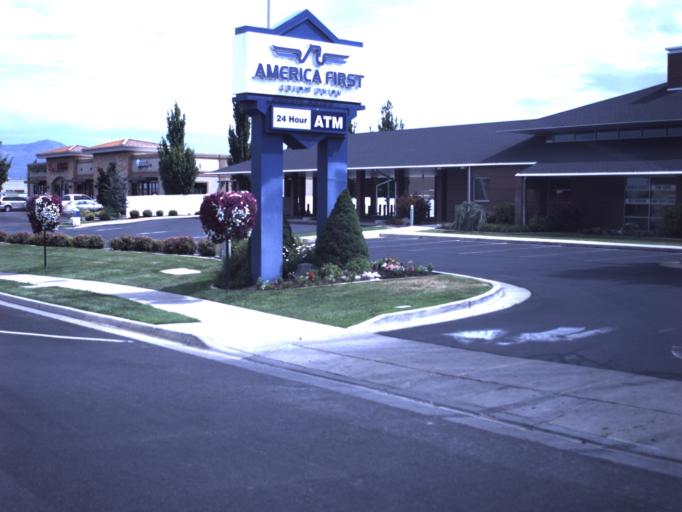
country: US
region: Utah
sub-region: Davis County
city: Clinton
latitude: 41.1385
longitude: -112.0644
